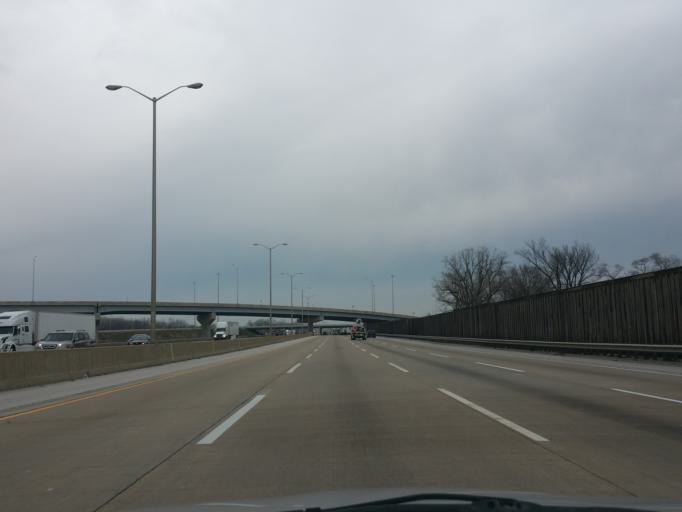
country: US
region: Illinois
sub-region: Cook County
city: Posen
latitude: 41.6140
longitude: -87.6843
